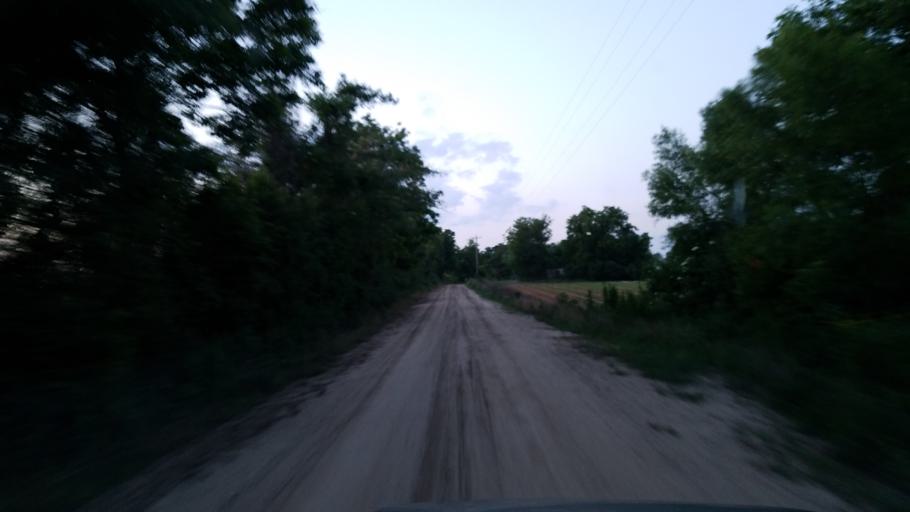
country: US
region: Georgia
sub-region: Turner County
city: Ashburn
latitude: 31.6572
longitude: -83.6275
